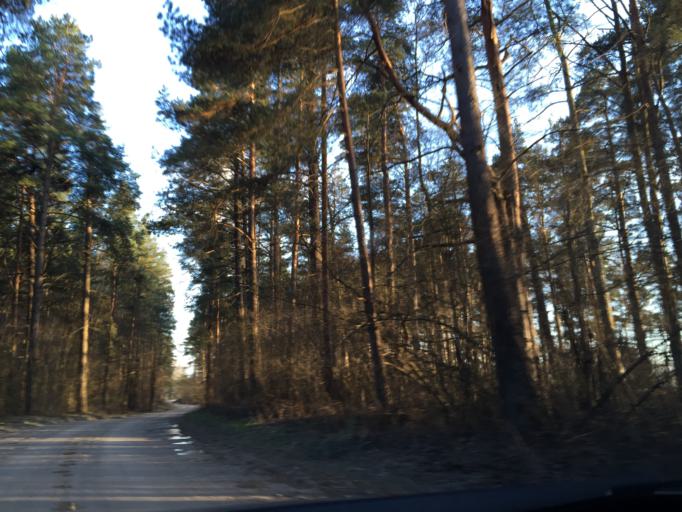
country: LV
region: Kekava
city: Kekava
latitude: 56.8533
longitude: 24.2242
